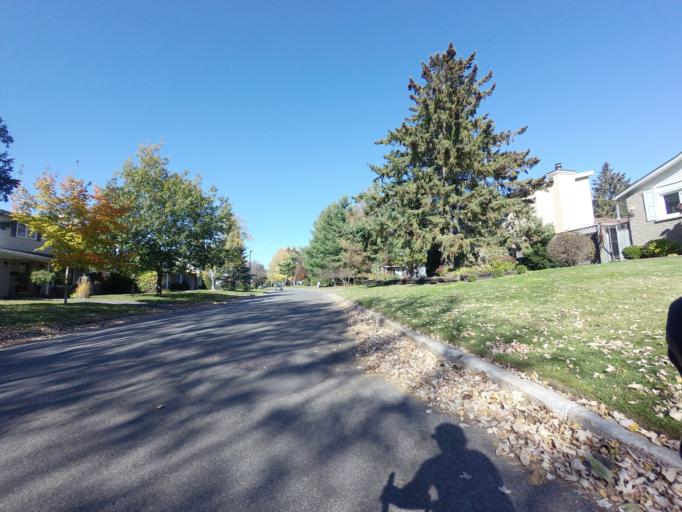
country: CA
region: Ontario
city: Bells Corners
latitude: 45.2943
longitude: -75.8748
